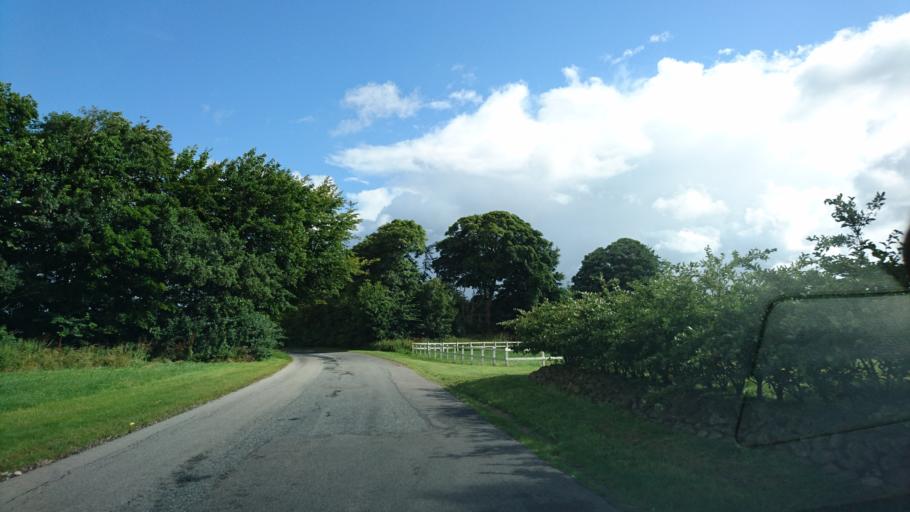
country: DK
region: North Denmark
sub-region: Hjorring Kommune
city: Sindal
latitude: 57.4205
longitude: 10.1961
